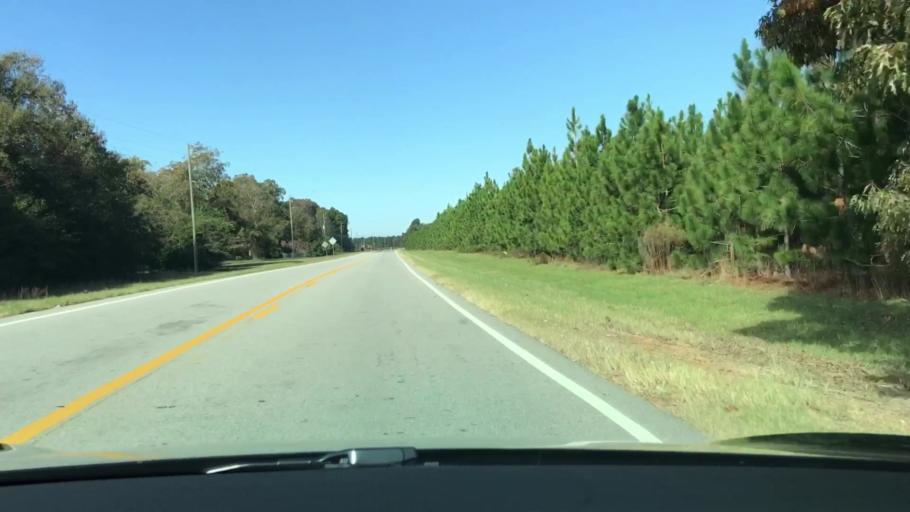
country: US
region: Georgia
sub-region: Glascock County
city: Gibson
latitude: 33.3081
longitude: -82.5326
